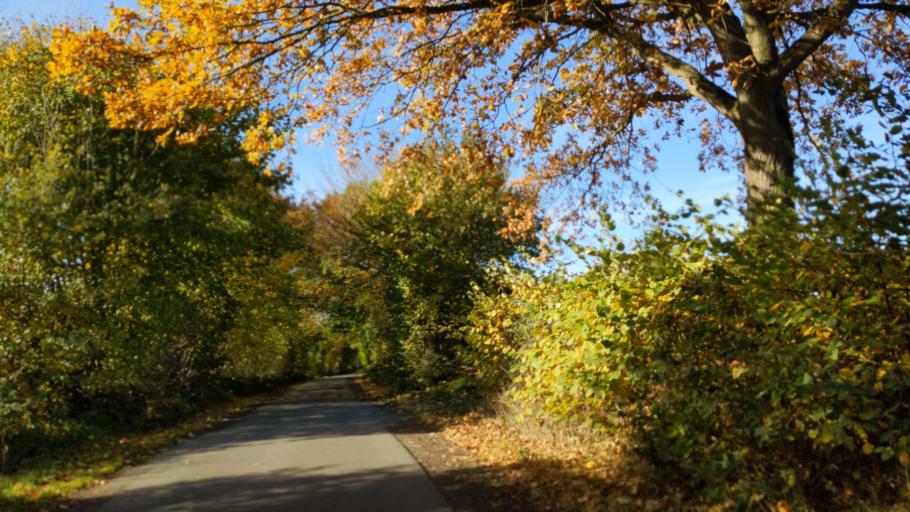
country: DE
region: Schleswig-Holstein
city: Kasseedorf
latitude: 54.1305
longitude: 10.7487
